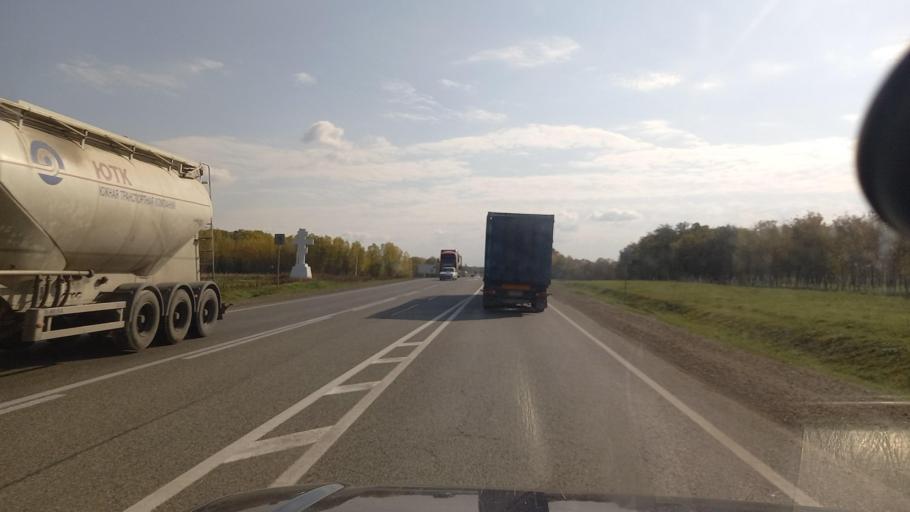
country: RU
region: Krasnodarskiy
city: Novoukrainskiy
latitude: 44.8876
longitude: 38.0798
